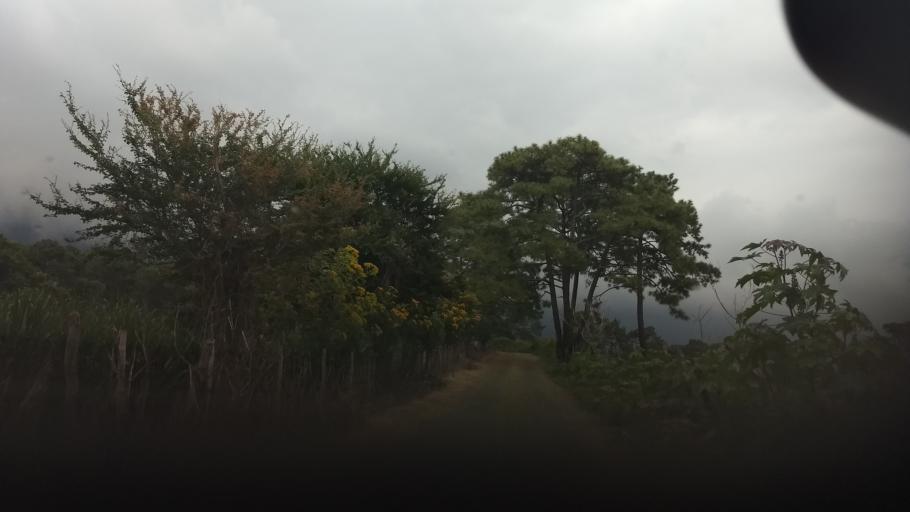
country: MX
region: Colima
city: Cofradia
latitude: 19.4685
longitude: -103.5379
